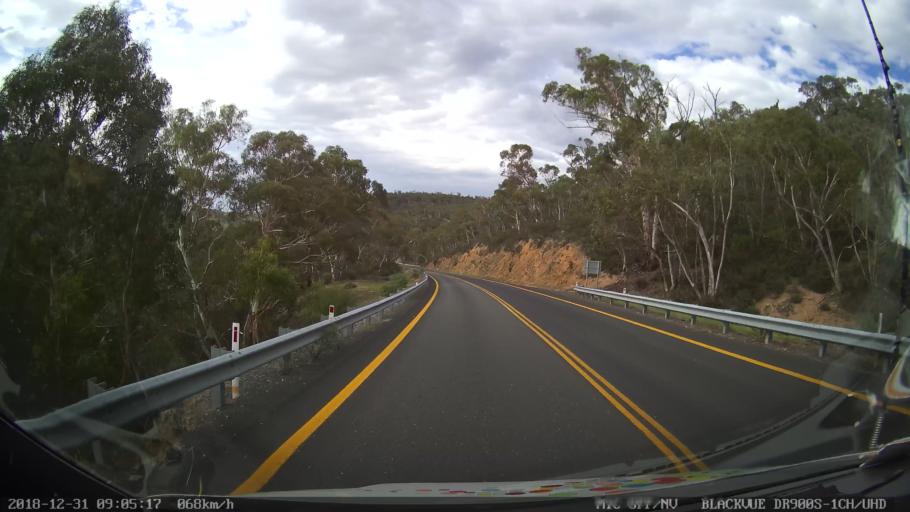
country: AU
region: New South Wales
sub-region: Snowy River
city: Jindabyne
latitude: -36.3617
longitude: 148.5873
